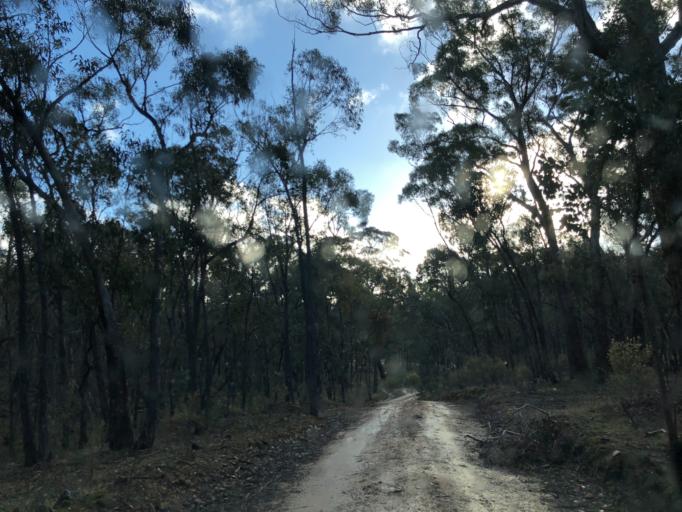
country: AU
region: Victoria
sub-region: Mount Alexander
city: Castlemaine
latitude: -37.2204
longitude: 144.2639
